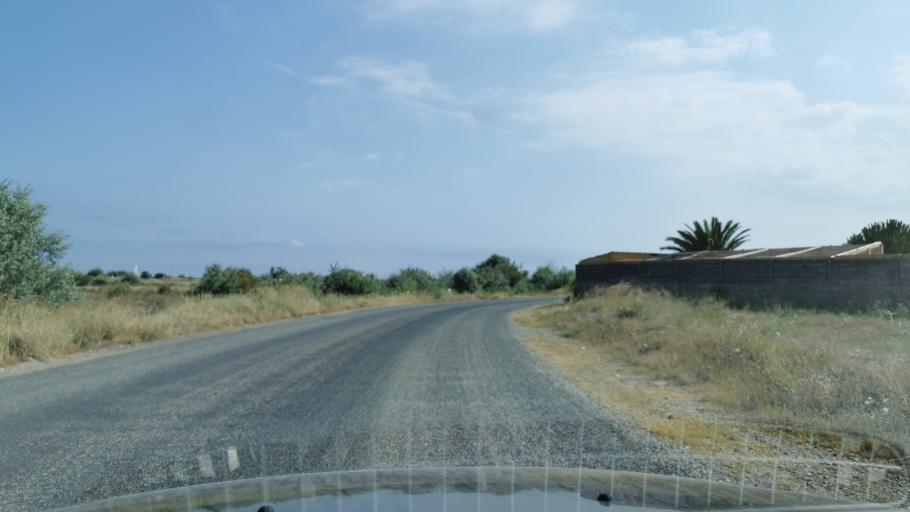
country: FR
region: Languedoc-Roussillon
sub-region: Departement de l'Aude
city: Gruissan
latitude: 43.1167
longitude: 3.1210
